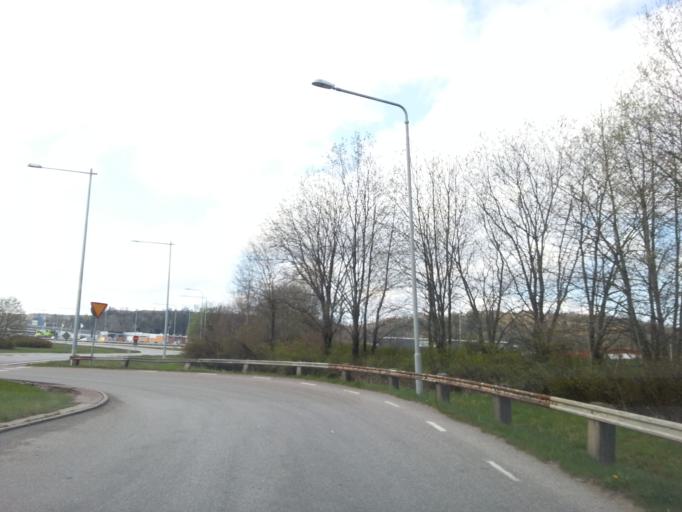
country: SE
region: Vaestra Goetaland
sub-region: Goteborg
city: Gardsten
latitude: 57.7864
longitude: 12.0023
